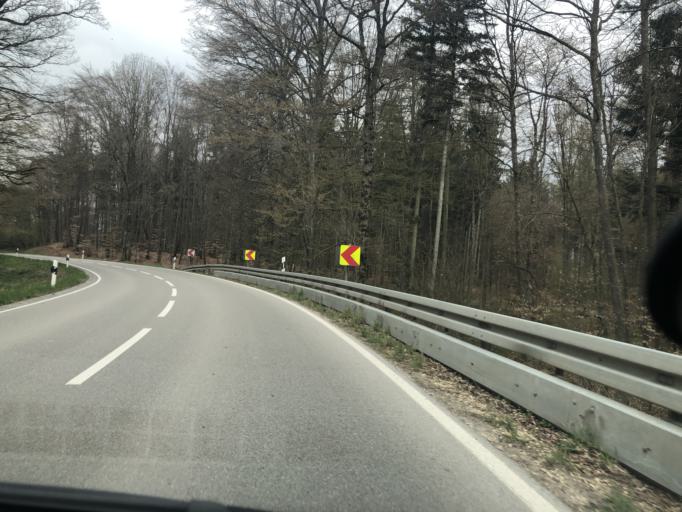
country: DE
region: Bavaria
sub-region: Upper Bavaria
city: Kirchdorf
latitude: 48.4416
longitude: 11.6769
